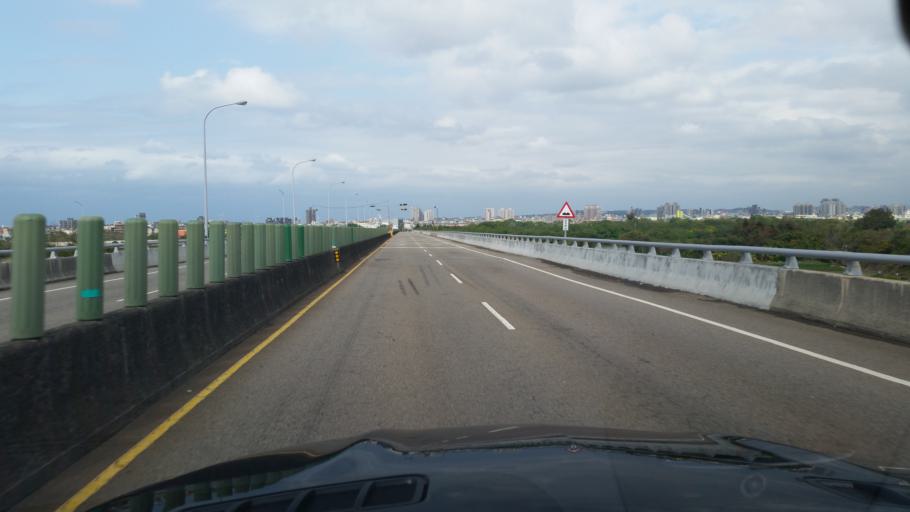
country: TW
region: Taiwan
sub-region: Miaoli
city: Miaoli
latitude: 24.6626
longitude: 120.8670
